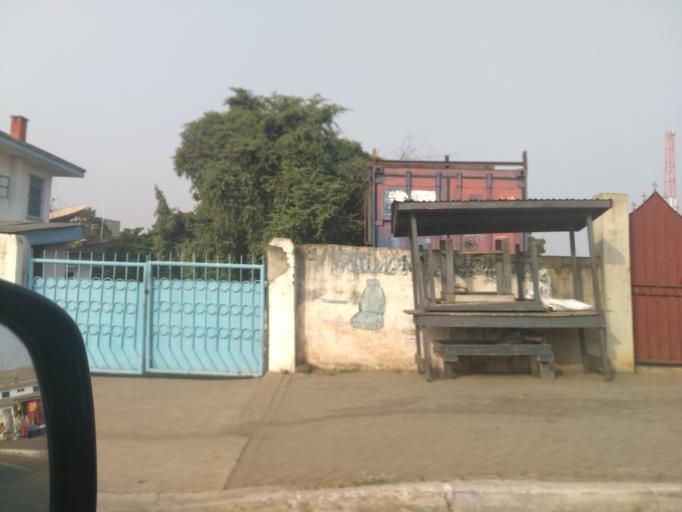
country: GH
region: Greater Accra
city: Accra
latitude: 5.5751
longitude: -0.2008
